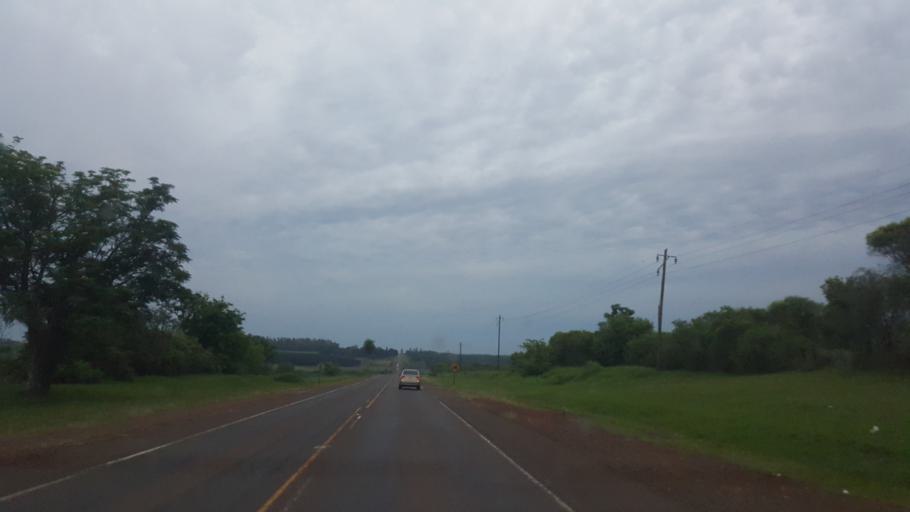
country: AR
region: Misiones
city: Garupa
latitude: -27.6069
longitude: -55.8233
